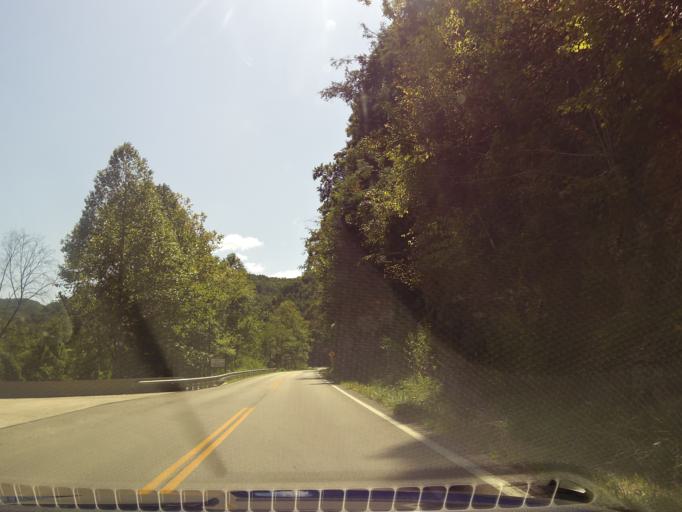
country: US
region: Kentucky
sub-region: Clay County
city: Manchester
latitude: 37.1616
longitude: -83.5711
